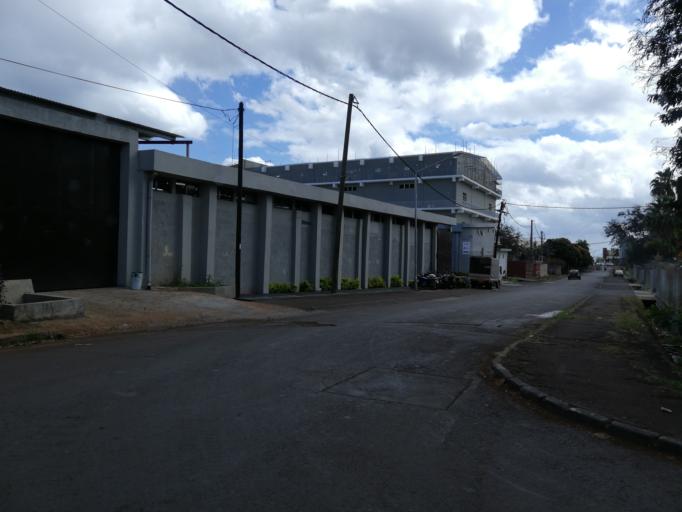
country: MU
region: Black River
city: Petite Riviere
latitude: -20.1914
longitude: 57.4657
